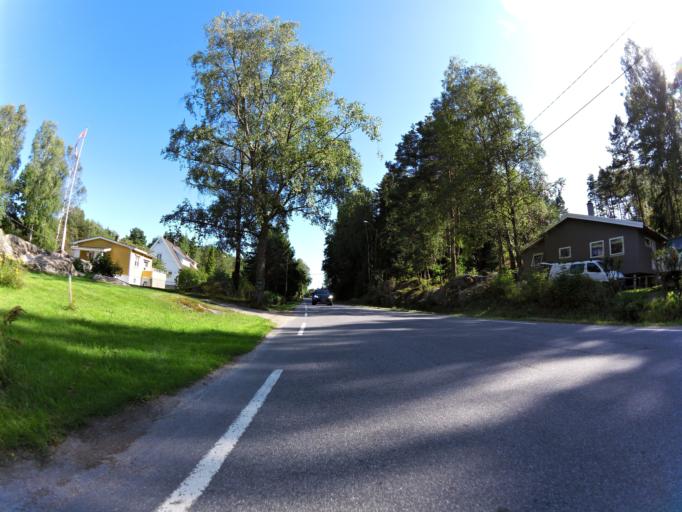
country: NO
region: Ostfold
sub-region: Fredrikstad
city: Fredrikstad
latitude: 59.1814
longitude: 10.8387
